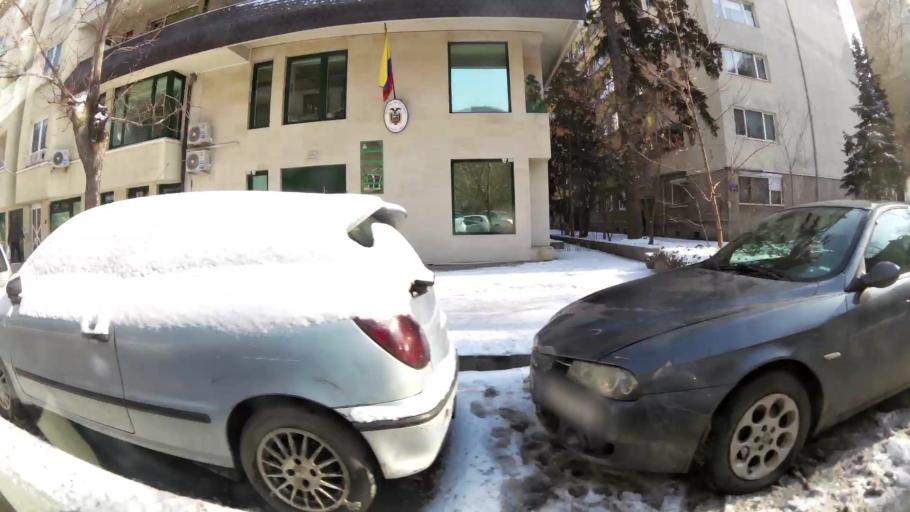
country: BG
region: Sofia-Capital
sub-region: Stolichna Obshtina
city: Sofia
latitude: 42.6756
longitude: 23.3081
